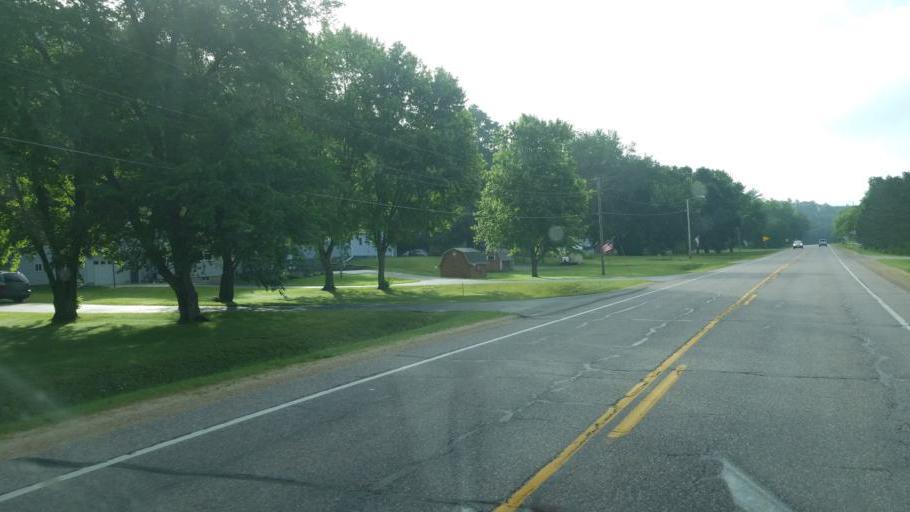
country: US
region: Wisconsin
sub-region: Juneau County
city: Elroy
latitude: 43.6804
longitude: -90.2600
